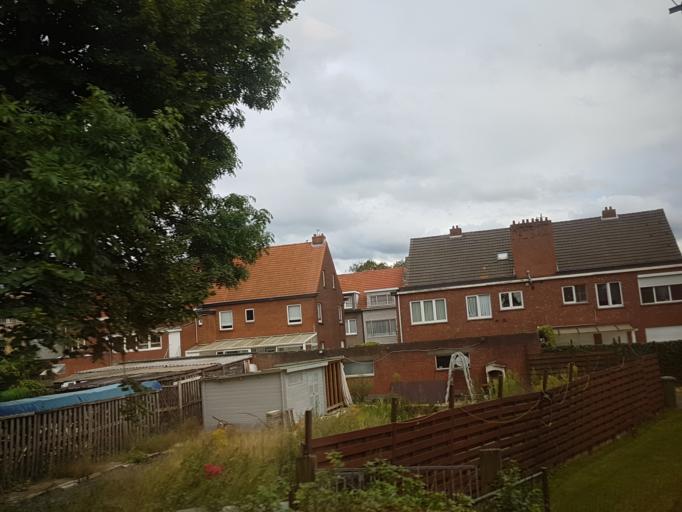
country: BE
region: Flanders
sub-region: Provincie Antwerpen
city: Kapellen
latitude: 51.2882
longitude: 4.4358
